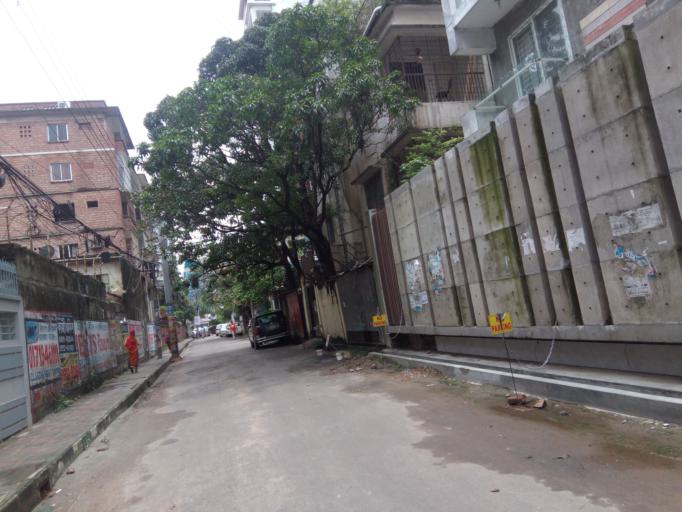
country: BD
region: Dhaka
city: Azimpur
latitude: 23.7529
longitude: 90.3684
